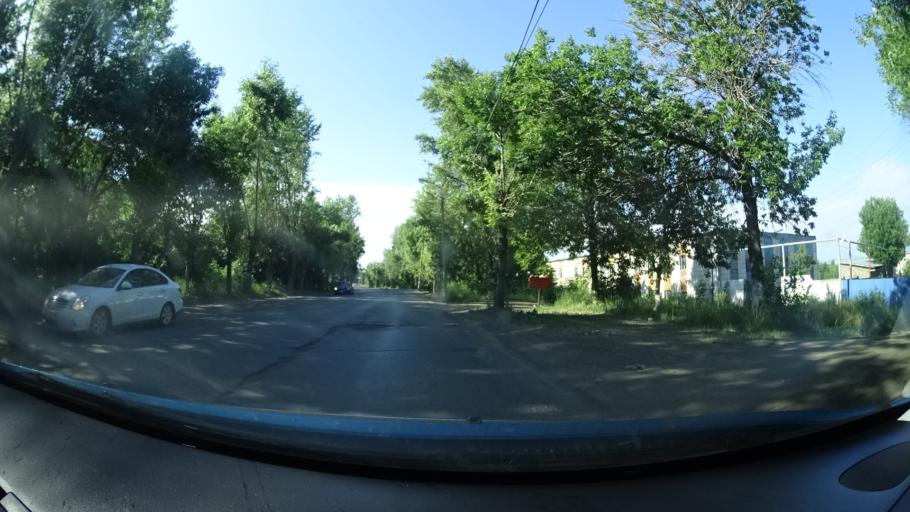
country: RU
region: Bashkortostan
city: Ufa
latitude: 54.8390
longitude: 56.0757
